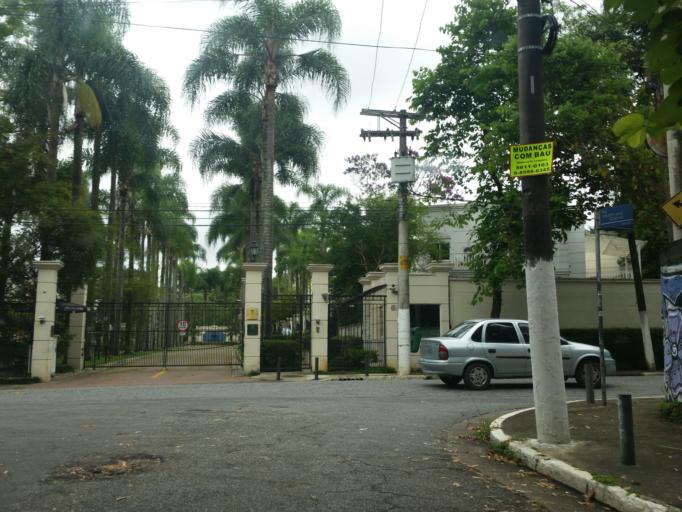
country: BR
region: Sao Paulo
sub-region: Diadema
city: Diadema
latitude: -23.6485
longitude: -46.6935
